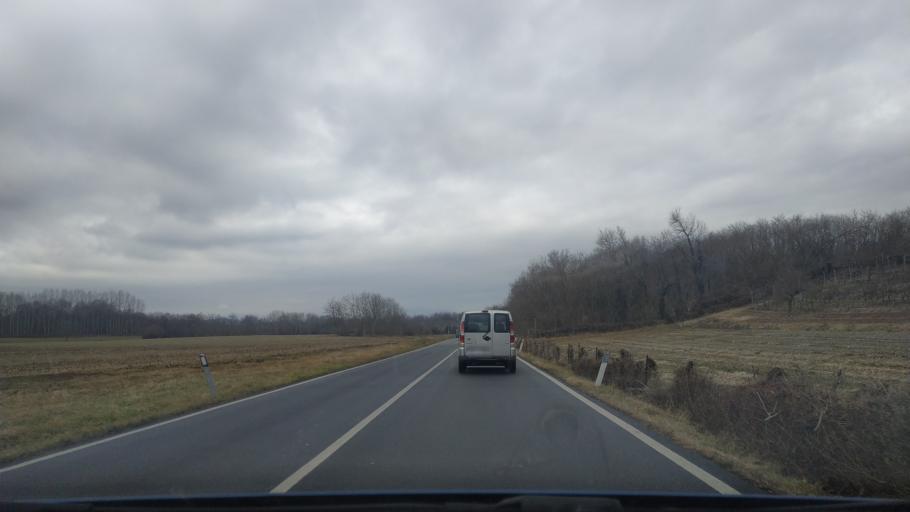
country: IT
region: Piedmont
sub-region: Provincia di Torino
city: Mercenasco
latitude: 45.3467
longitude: 7.8844
